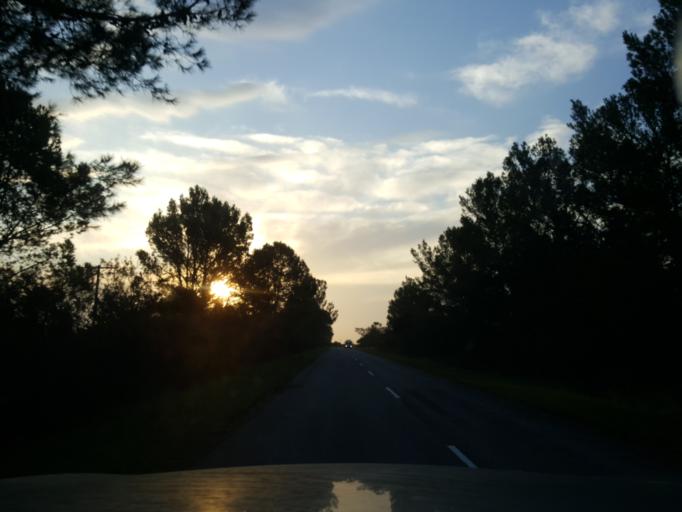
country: ZA
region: Eastern Cape
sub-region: Cacadu District Municipality
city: Grahamstown
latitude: -33.4539
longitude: 26.4930
